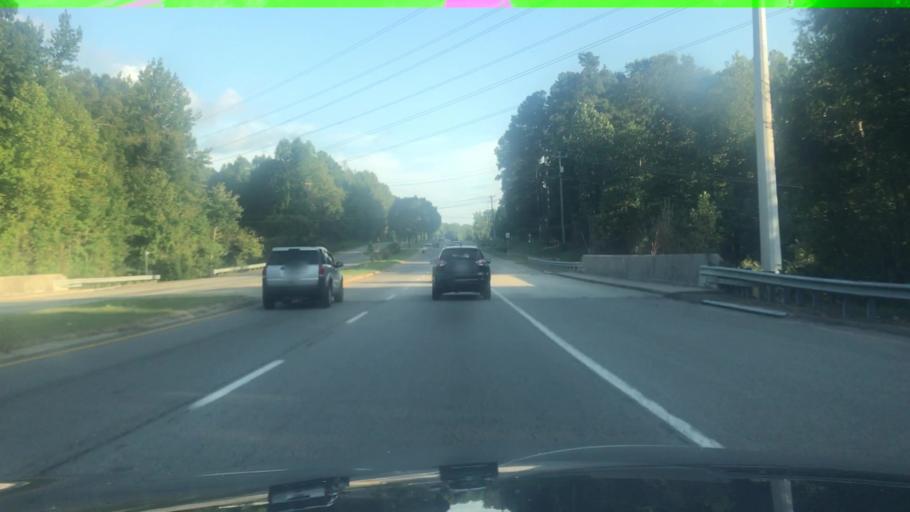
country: US
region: Virginia
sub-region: Chesterfield County
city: Brandermill
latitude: 37.4547
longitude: -77.5883
